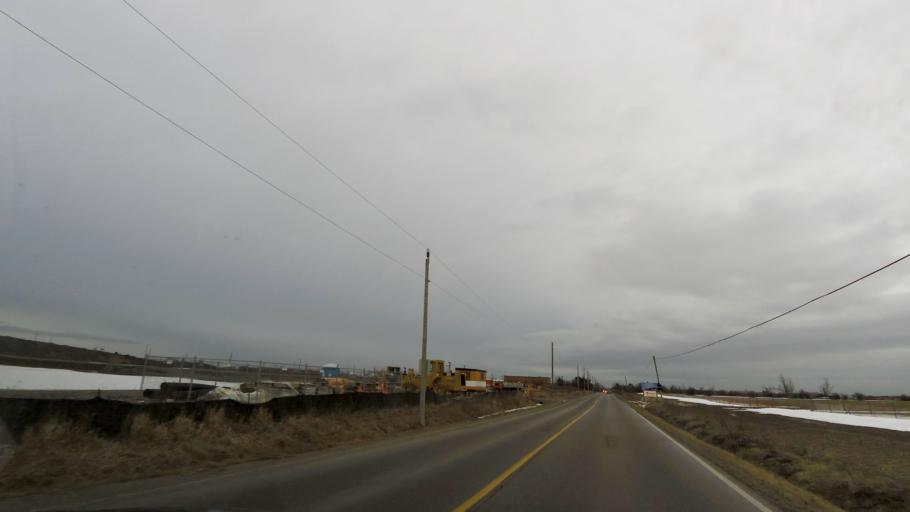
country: CA
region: Ontario
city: Brampton
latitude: 43.8250
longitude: -79.6871
